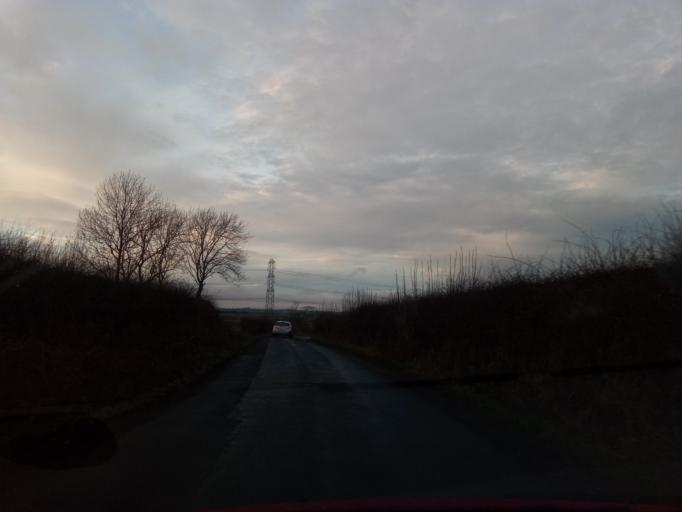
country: GB
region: England
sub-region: Northumberland
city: Ponteland
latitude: 55.0765
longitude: -1.7356
